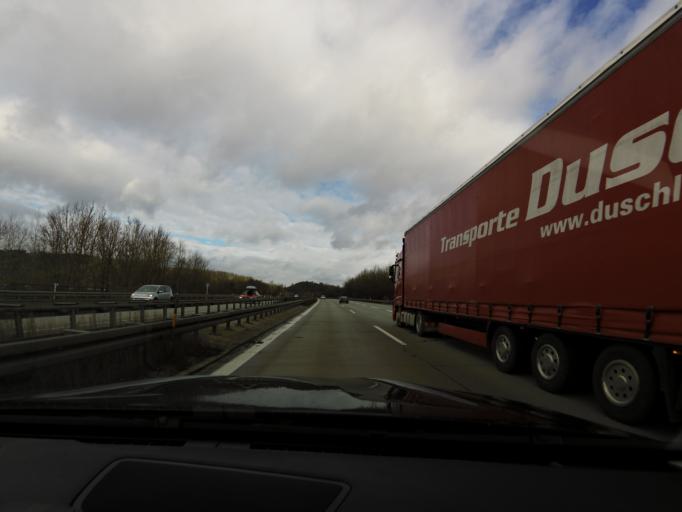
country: DE
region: Bavaria
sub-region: Lower Bavaria
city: Eching
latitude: 48.5328
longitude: 12.0716
